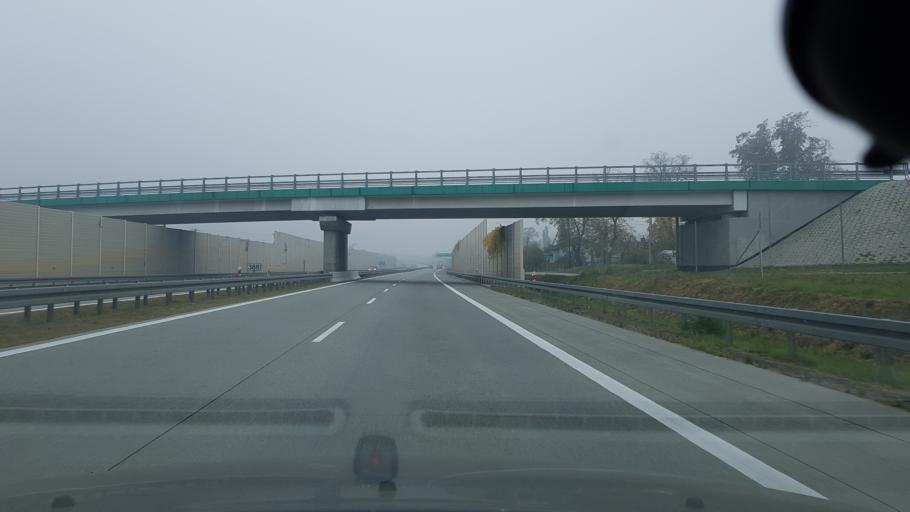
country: PL
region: Lodz Voivodeship
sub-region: Powiat rawski
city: Rawa Mazowiecka
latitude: 51.7896
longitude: 20.2858
